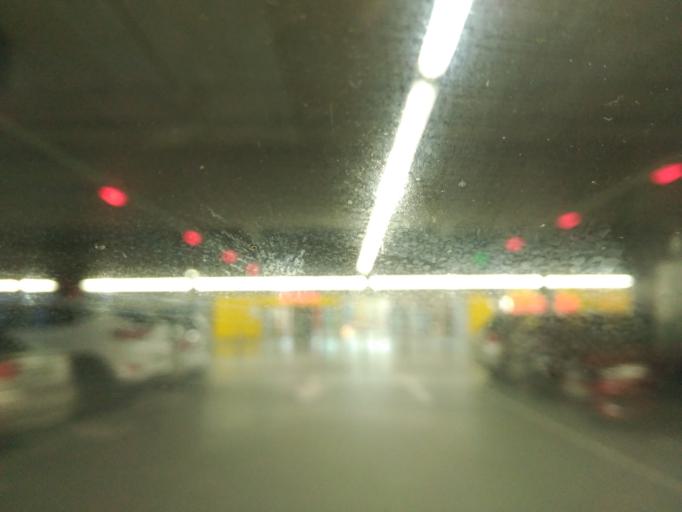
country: ES
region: Castille and Leon
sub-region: Provincia de Valladolid
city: Arroyo
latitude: 41.6273
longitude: -4.7882
